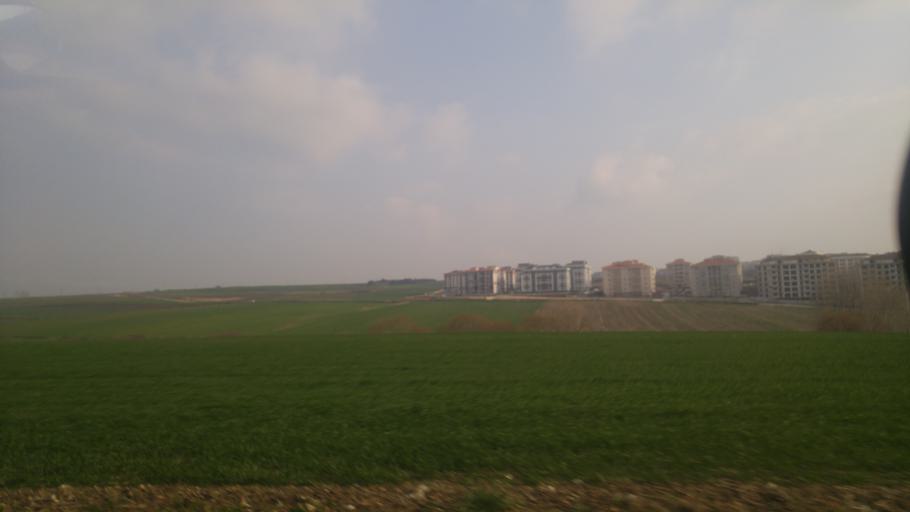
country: TR
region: Istanbul
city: Silivri
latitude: 41.0877
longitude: 28.2685
